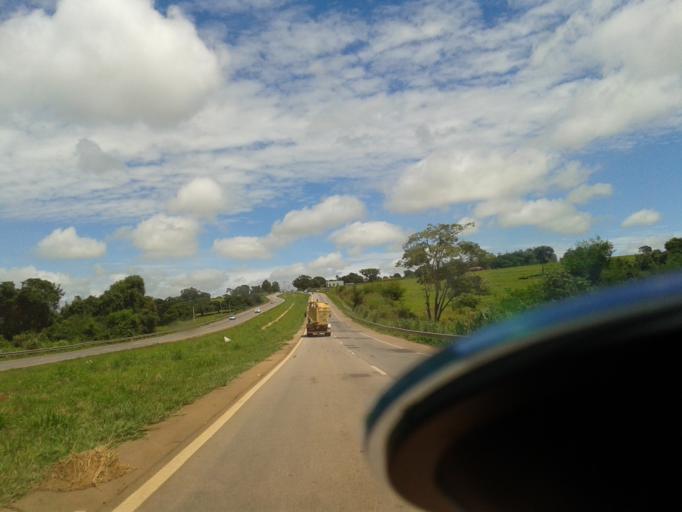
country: BR
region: Goias
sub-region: Inhumas
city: Inhumas
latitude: -16.2774
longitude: -49.5431
